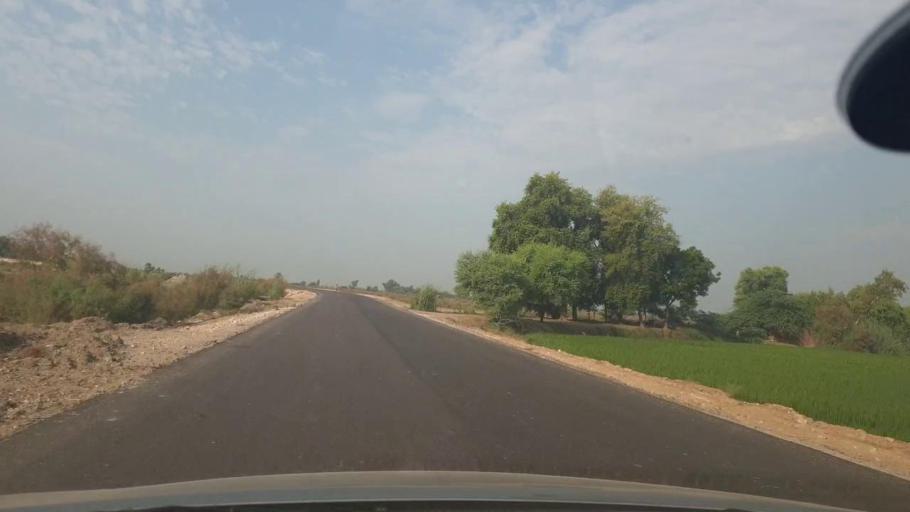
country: PK
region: Sindh
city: Jacobabad
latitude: 28.1287
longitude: 68.3305
